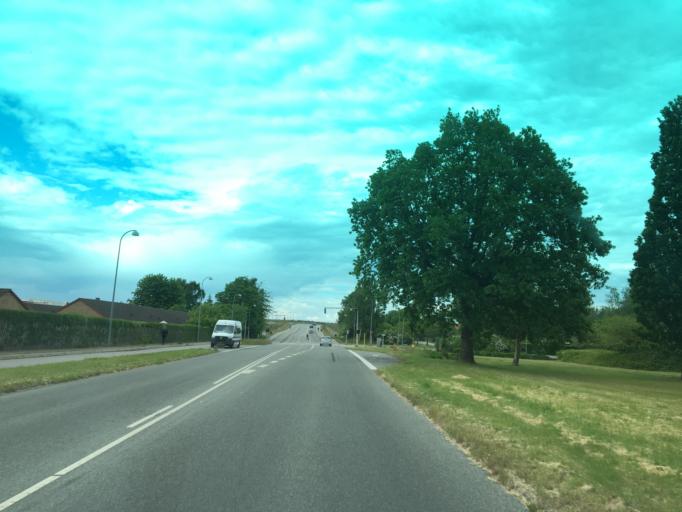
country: DK
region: Capital Region
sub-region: Hvidovre Kommune
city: Hvidovre
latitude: 55.6432
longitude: 12.4455
